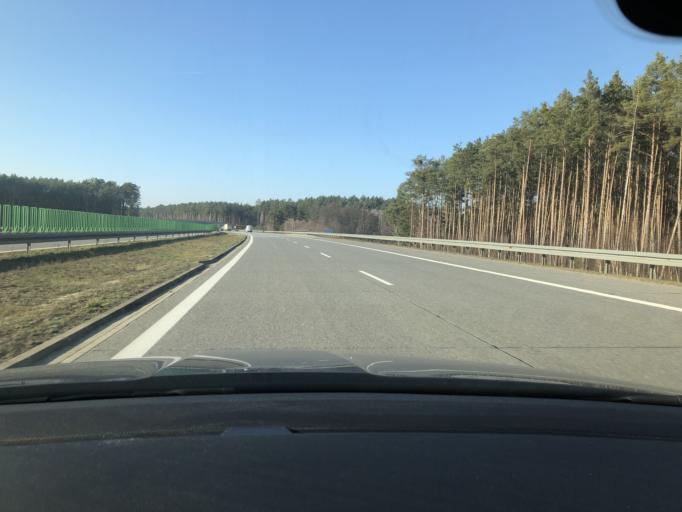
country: PL
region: Lubusz
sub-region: Powiat swiebodzinski
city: Lagow
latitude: 52.3068
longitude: 15.2503
